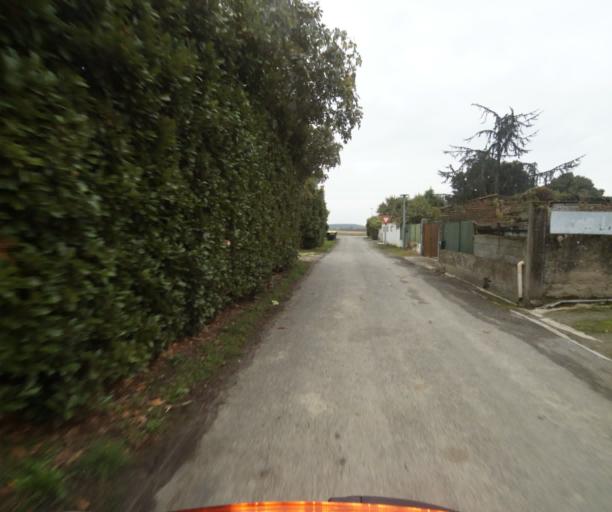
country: FR
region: Midi-Pyrenees
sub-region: Departement du Tarn-et-Garonne
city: Verdun-sur-Garonne
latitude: 43.8588
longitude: 1.2554
